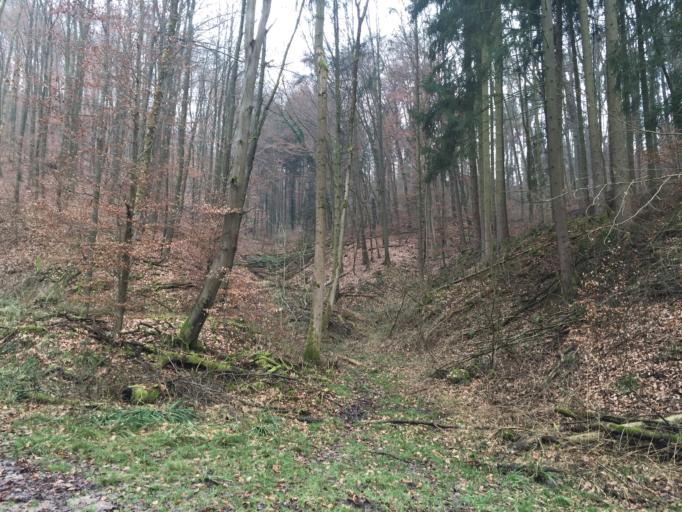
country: DE
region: Hesse
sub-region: Regierungsbezirk Darmstadt
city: Birkenau
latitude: 49.5749
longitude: 8.6900
